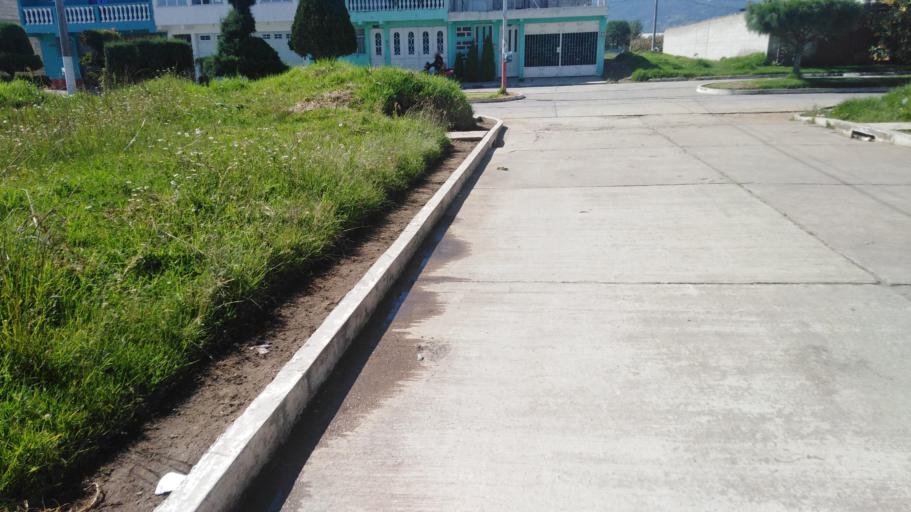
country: GT
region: Quetzaltenango
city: Olintepeque
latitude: 14.8651
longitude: -91.5087
